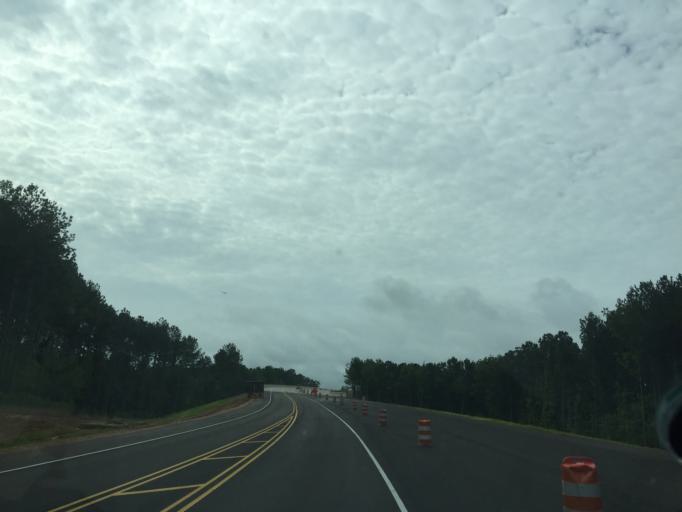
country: US
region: Mississippi
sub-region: Rankin County
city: Brandon
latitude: 32.2916
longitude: -89.9958
